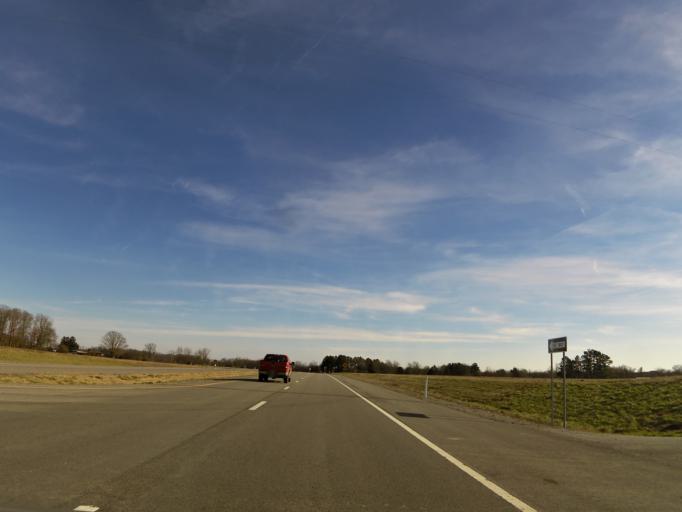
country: US
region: Tennessee
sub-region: Cannon County
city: Woodbury
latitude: 35.7708
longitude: -85.9765
